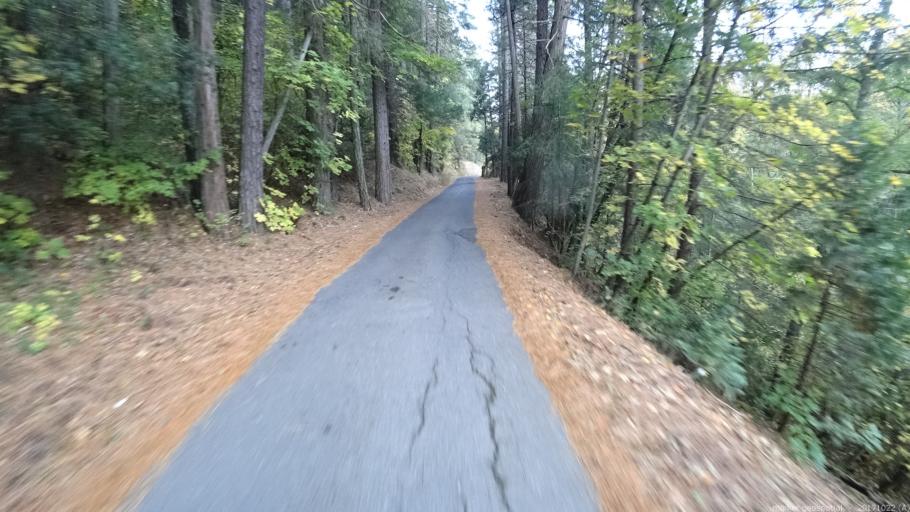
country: US
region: California
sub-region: Siskiyou County
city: Dunsmuir
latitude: 41.1681
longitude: -122.2839
